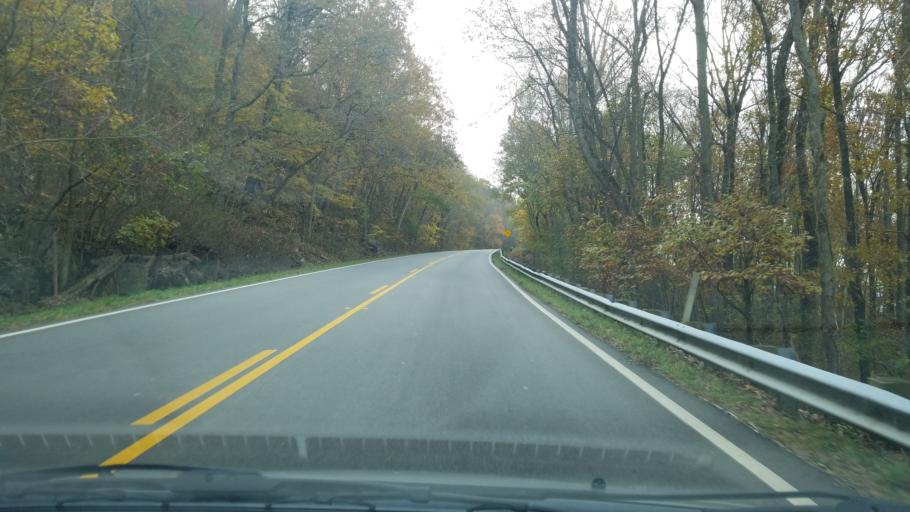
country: US
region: Georgia
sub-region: Dade County
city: Trenton
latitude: 34.8333
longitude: -85.5006
